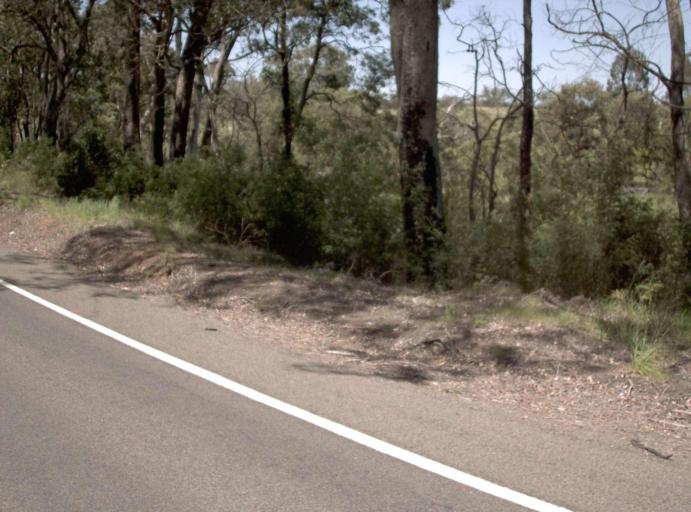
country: AU
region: Victoria
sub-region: East Gippsland
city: Lakes Entrance
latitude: -37.7521
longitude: 148.1920
